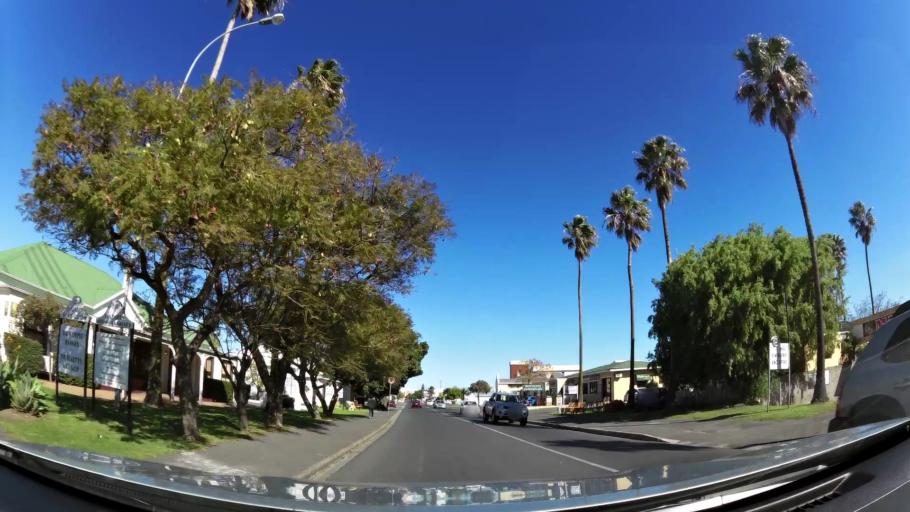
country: ZA
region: Western Cape
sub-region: Cape Winelands District Municipality
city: Stellenbosch
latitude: -34.1108
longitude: 18.8349
